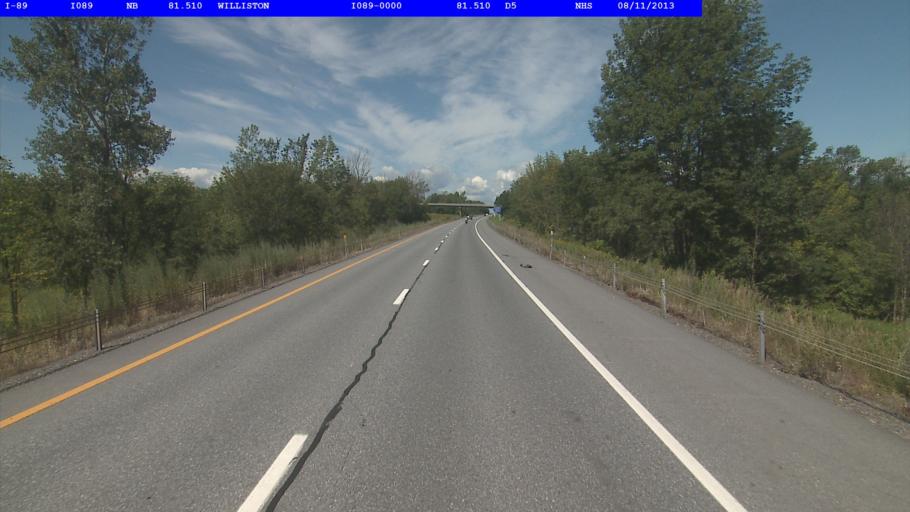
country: US
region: Vermont
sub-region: Chittenden County
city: Williston
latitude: 44.4339
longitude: -73.0662
